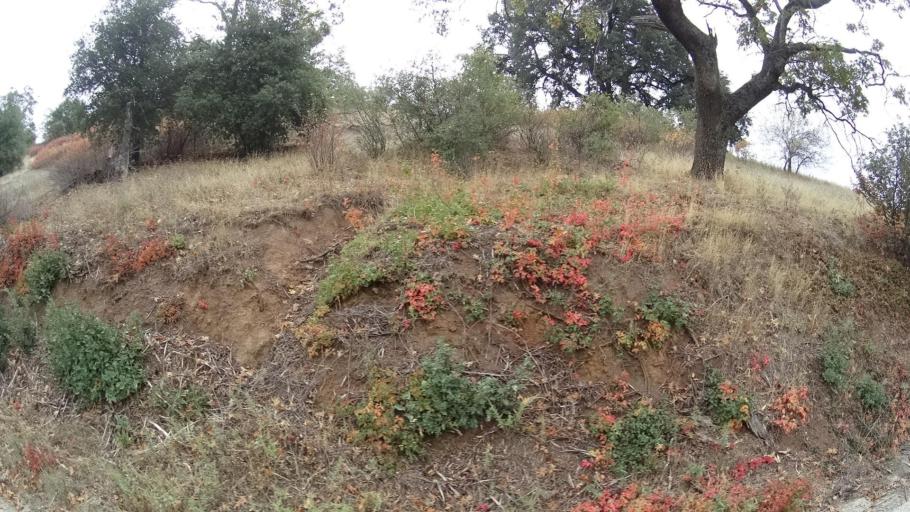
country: US
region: California
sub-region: San Diego County
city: Julian
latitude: 33.0319
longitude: -116.6563
